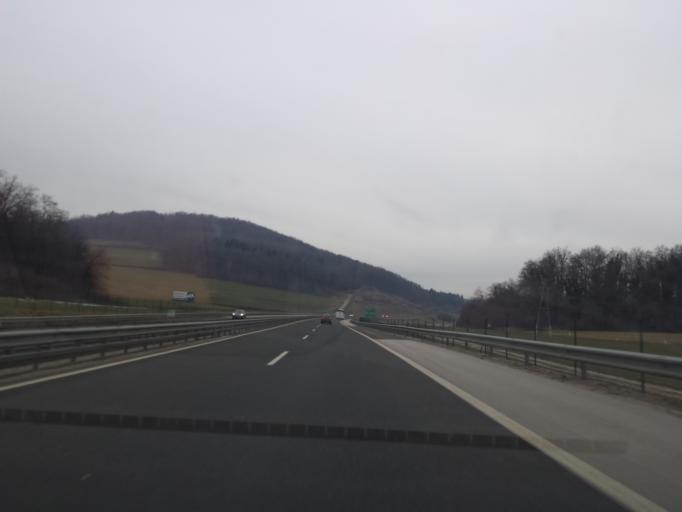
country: SI
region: Mirna Pec
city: Mirna Pec
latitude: 45.8676
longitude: 15.1209
